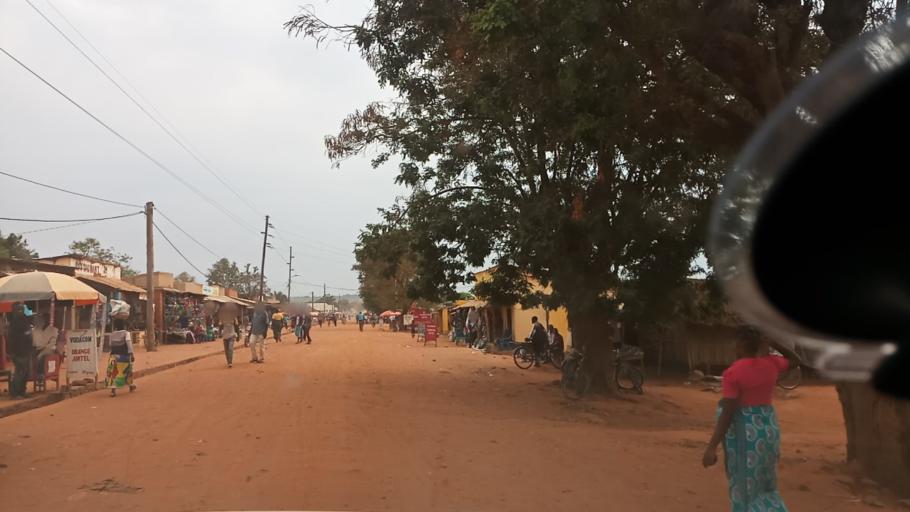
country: ZM
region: Northern
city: Kaputa
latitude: -8.4658
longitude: 28.8996
